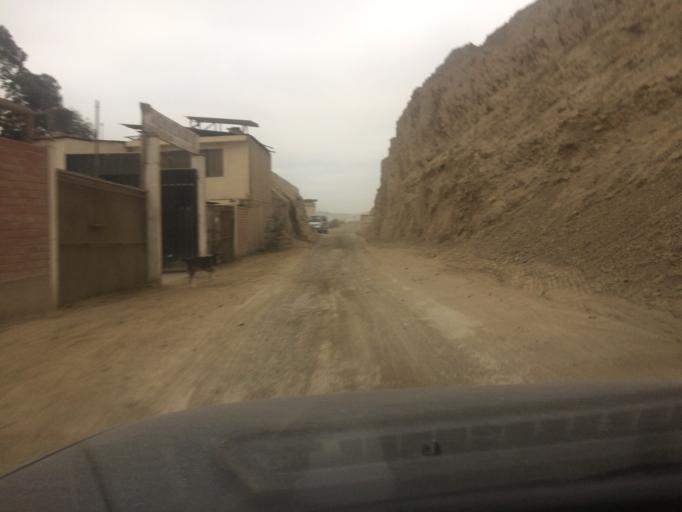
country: PE
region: Lima
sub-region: Lima
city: Cieneguilla
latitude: -12.2214
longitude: -76.8840
